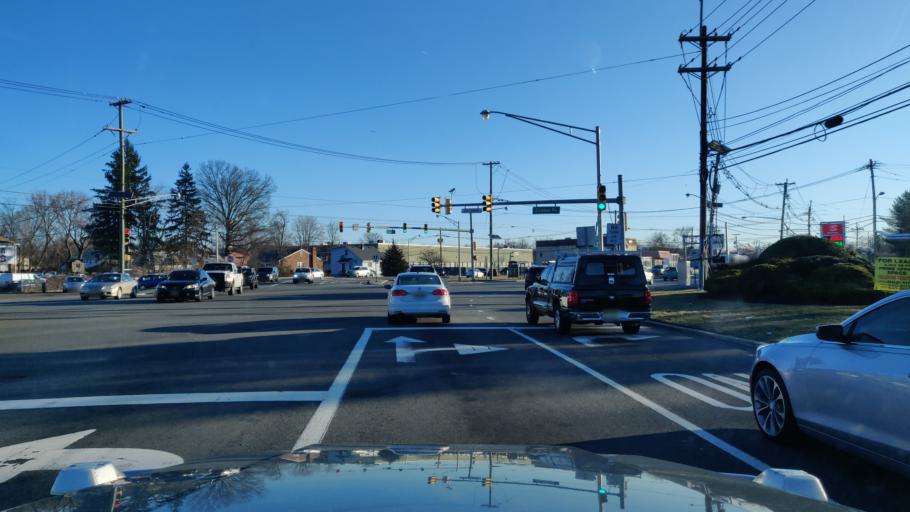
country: US
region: New Jersey
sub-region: Essex County
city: Fairfield
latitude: 40.8677
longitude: -74.3119
